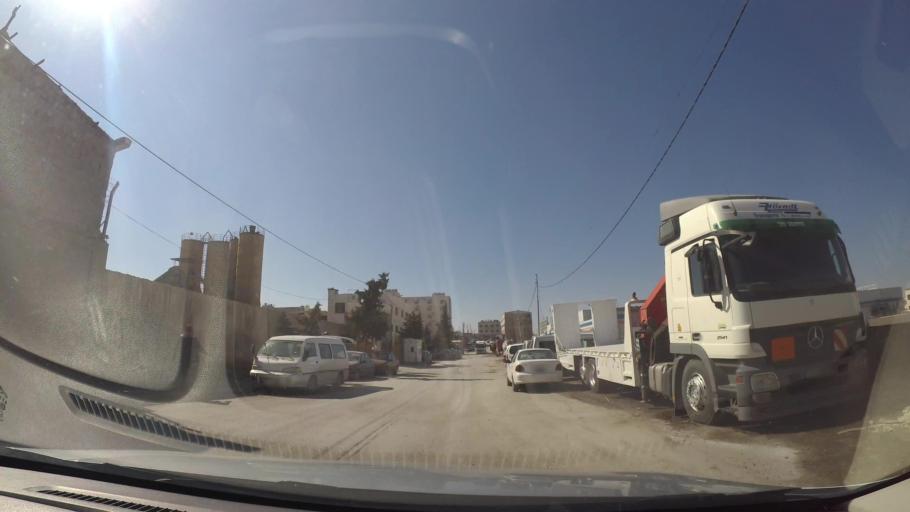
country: JO
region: Amman
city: Al Bunayyat ash Shamaliyah
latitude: 31.9148
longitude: 35.9111
